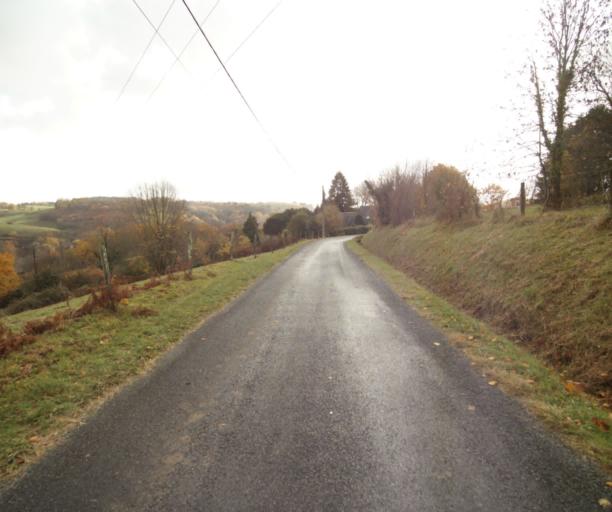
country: FR
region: Limousin
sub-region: Departement de la Correze
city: Sainte-Fereole
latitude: 45.2090
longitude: 1.6222
